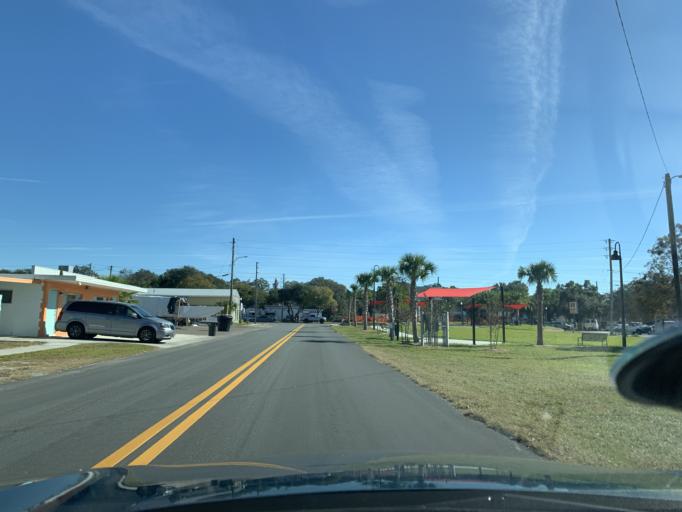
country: US
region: Florida
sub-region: Pinellas County
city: Gulfport
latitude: 27.7521
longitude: -82.7009
